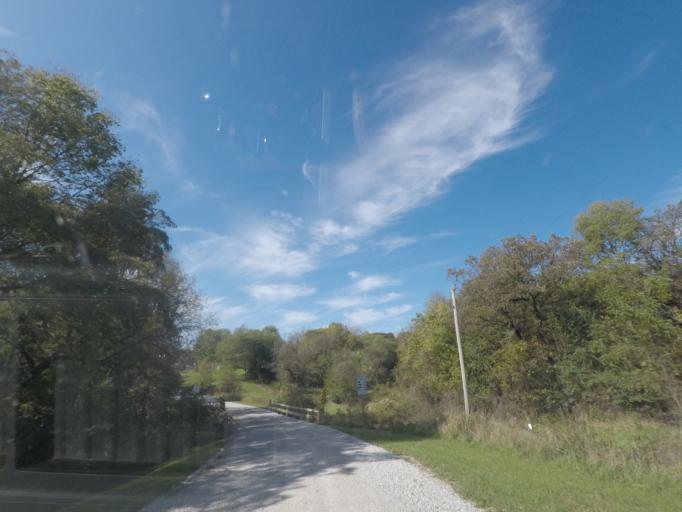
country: US
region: Iowa
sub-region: Story County
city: Nevada
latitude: 42.0127
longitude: -93.3522
